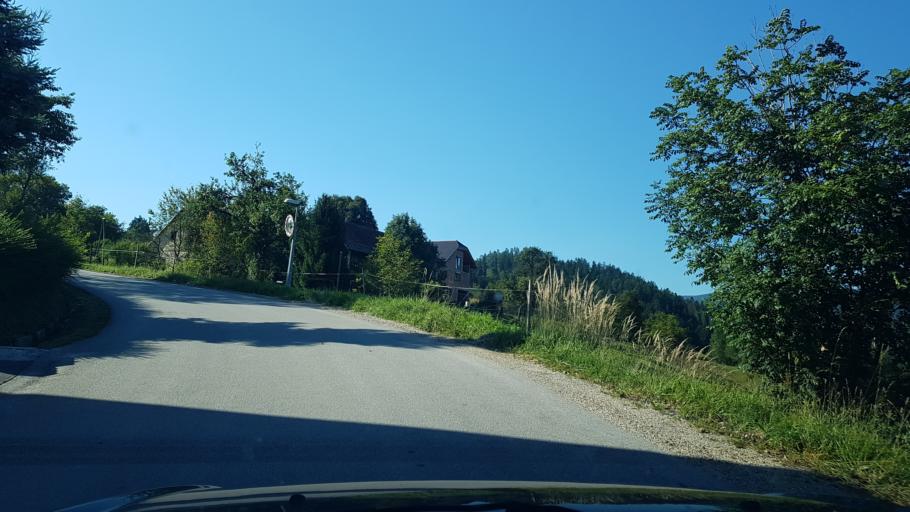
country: SI
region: Ravne na Koroskem
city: Kotlje
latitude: 46.5224
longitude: 14.9830
